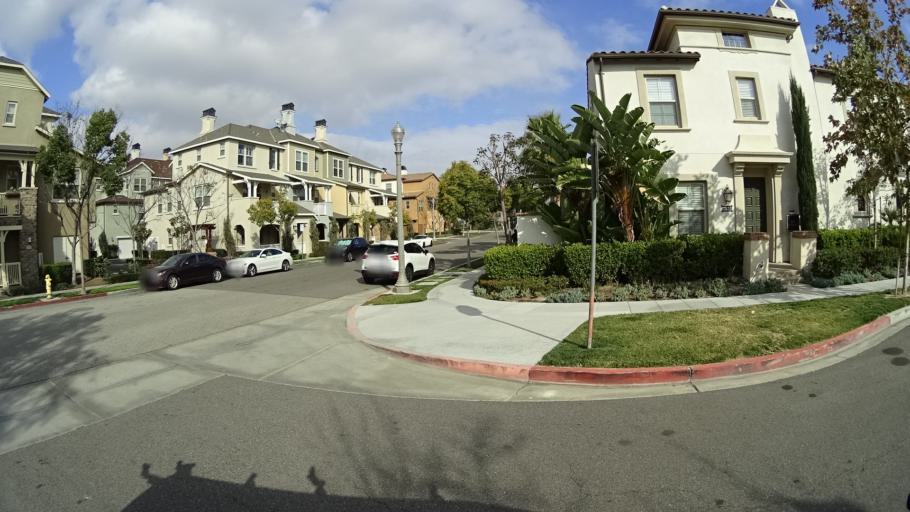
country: US
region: California
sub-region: Orange County
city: Anaheim
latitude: 33.8293
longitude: -117.9054
